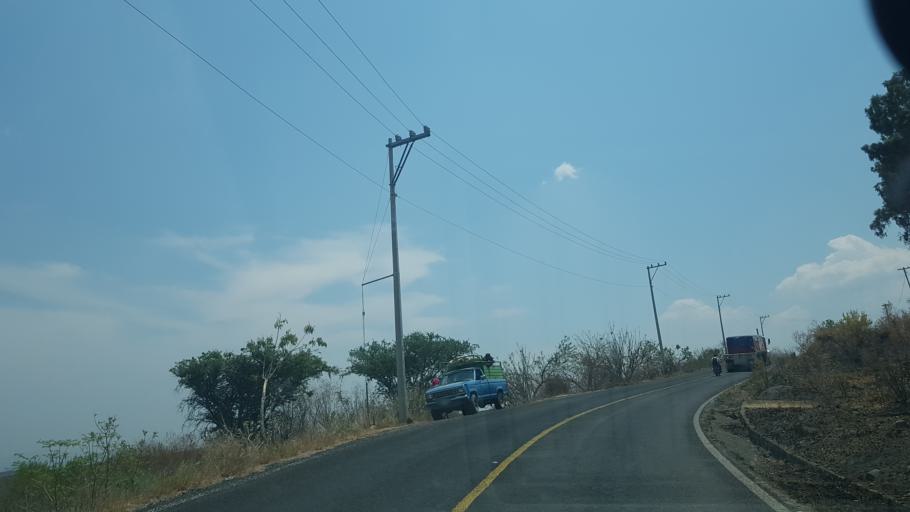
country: MX
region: Puebla
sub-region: Atzitzihuacan
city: Santiago Atzitzihuacan
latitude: 18.8340
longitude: -98.5878
